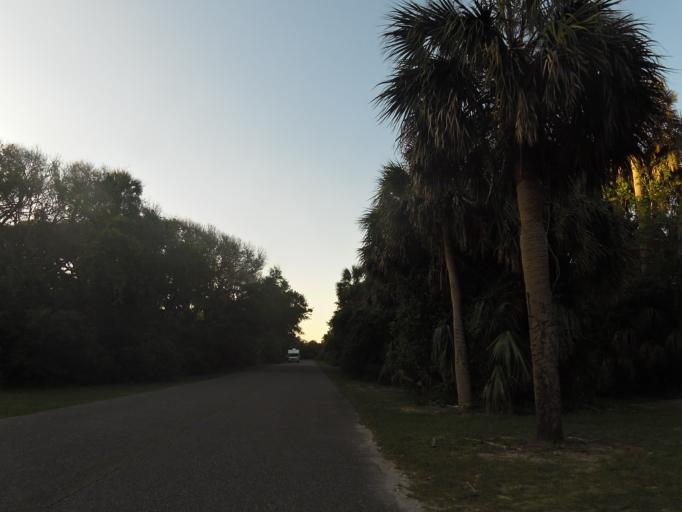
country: US
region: Florida
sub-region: Duval County
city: Atlantic Beach
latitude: 30.3724
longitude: -81.3997
